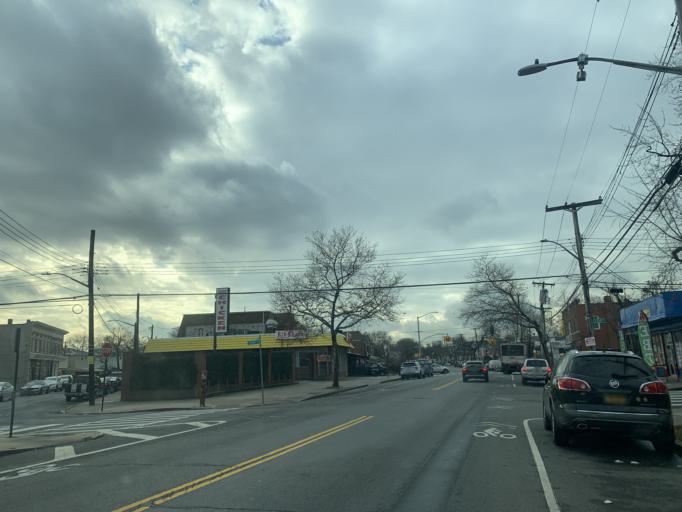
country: US
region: New York
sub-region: Queens County
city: Jamaica
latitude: 40.6881
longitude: -73.7894
